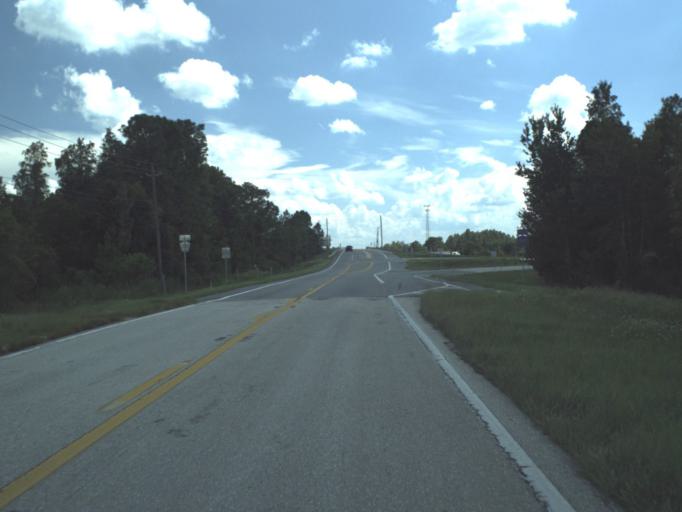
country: US
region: Florida
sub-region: Polk County
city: Polk City
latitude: 28.1855
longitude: -81.7457
